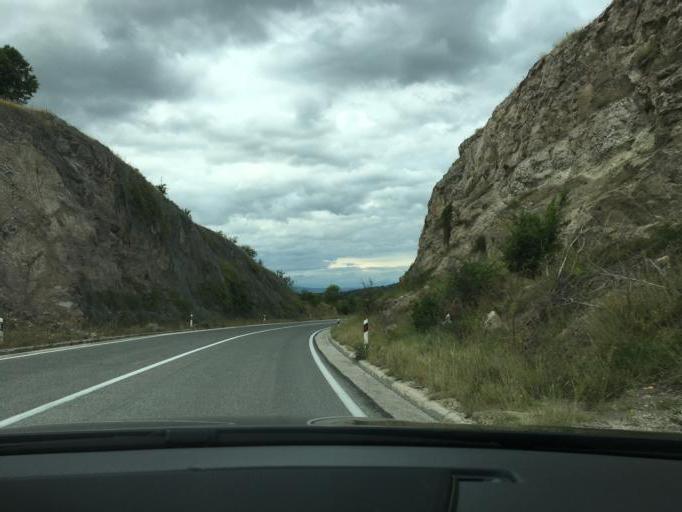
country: MK
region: Opstina Rankovce
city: Rankovce
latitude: 42.1454
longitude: 21.9943
